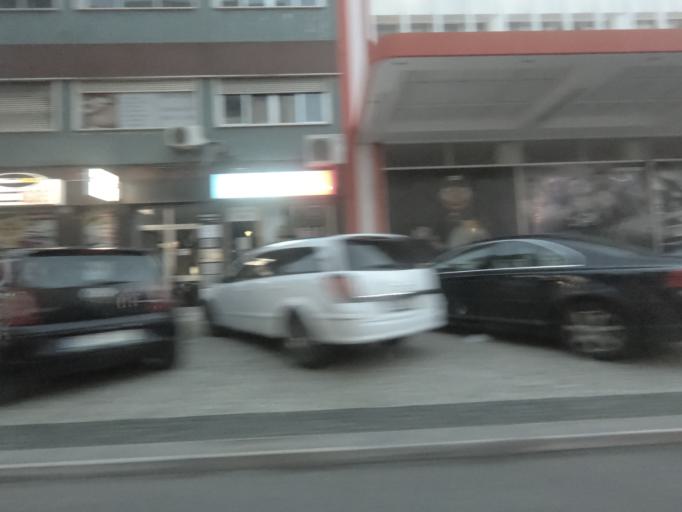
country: PT
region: Setubal
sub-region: Setubal
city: Setubal
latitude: 38.5254
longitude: -8.8917
